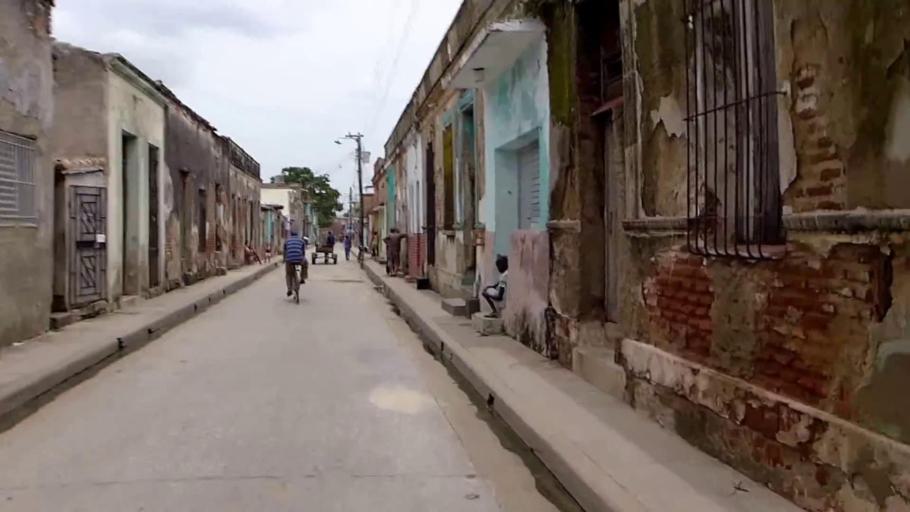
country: CU
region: Camaguey
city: Camaguey
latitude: 21.3807
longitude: -77.9239
